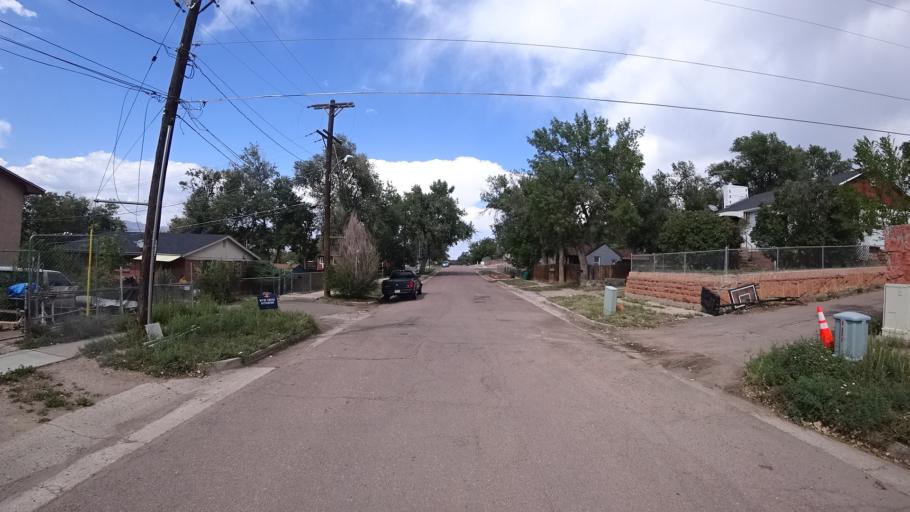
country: US
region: Colorado
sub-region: El Paso County
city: Colorado Springs
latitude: 38.8284
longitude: -104.8107
